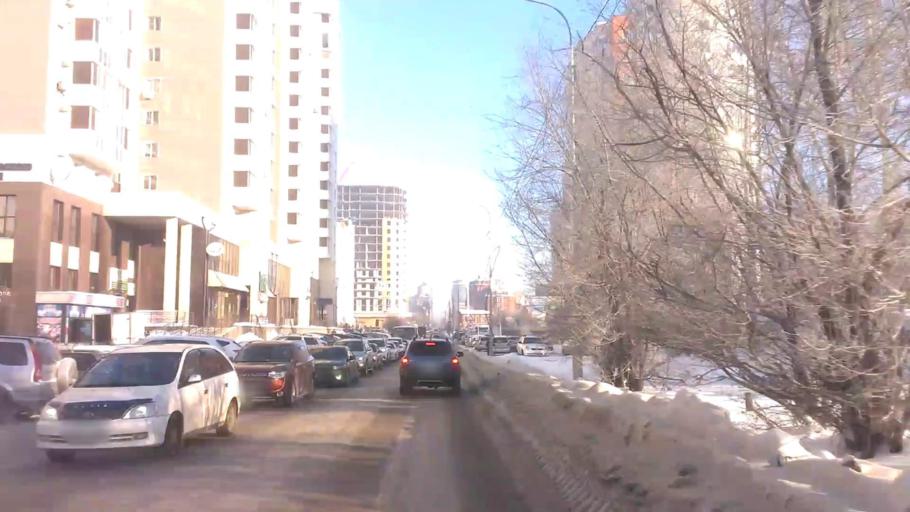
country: RU
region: Altai Krai
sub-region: Gorod Barnaulskiy
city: Barnaul
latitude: 53.3367
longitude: 83.7775
